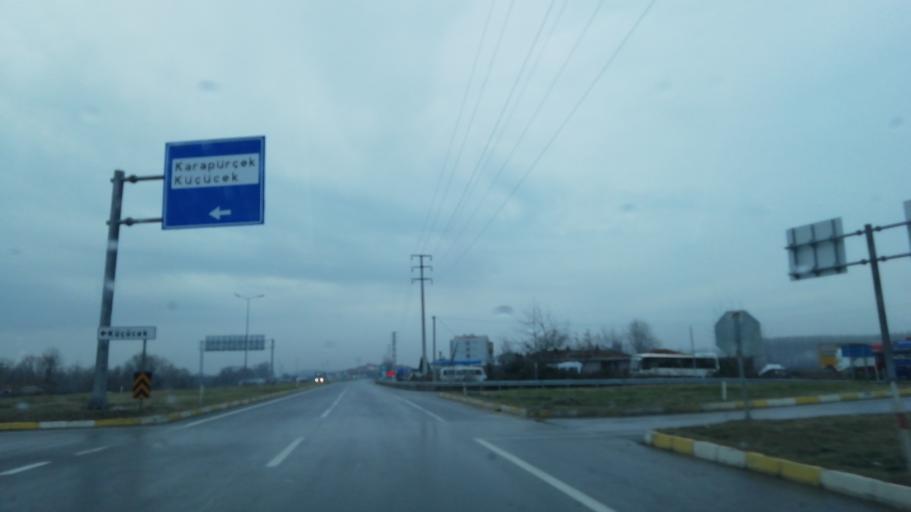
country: TR
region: Sakarya
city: Akyazi
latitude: 40.6595
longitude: 30.5971
